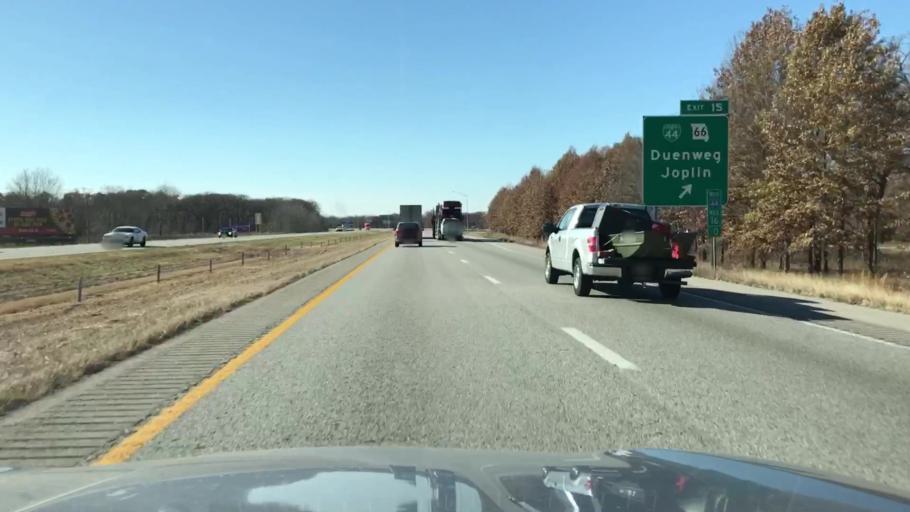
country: US
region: Missouri
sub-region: Jasper County
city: Duenweg
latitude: 37.0823
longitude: -94.3573
